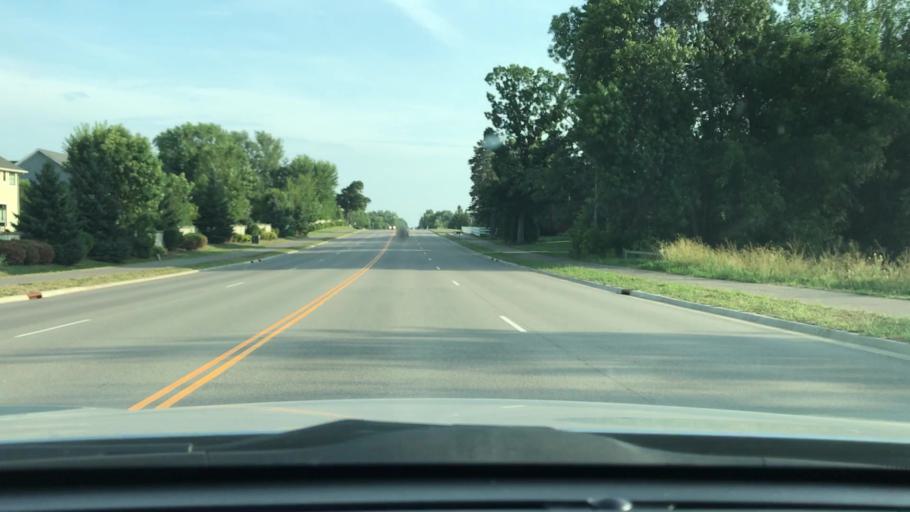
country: US
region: Minnesota
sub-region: Hennepin County
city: Maple Grove
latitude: 45.0489
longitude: -93.4818
